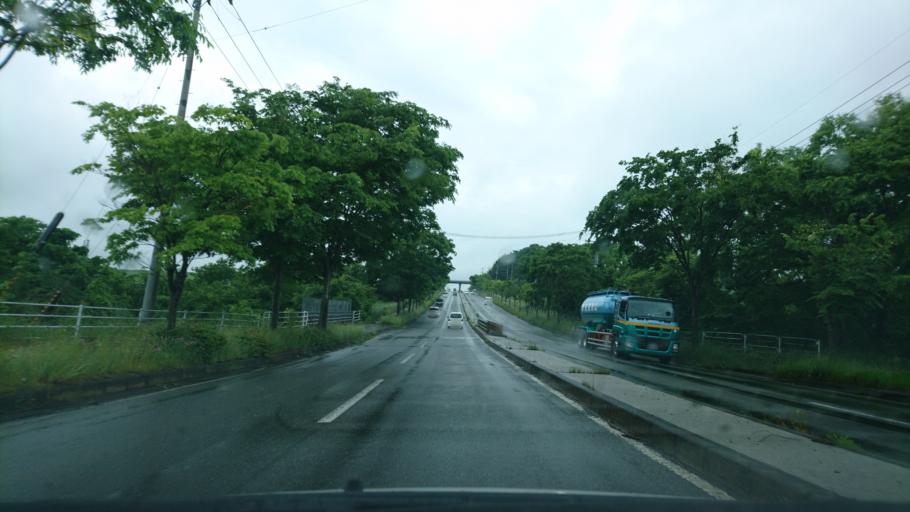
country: JP
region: Iwate
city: Ichinoseki
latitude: 38.9130
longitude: 141.1594
